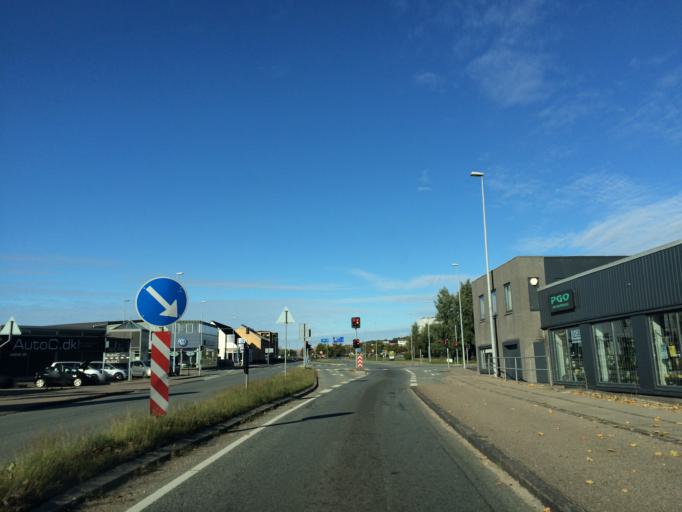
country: DK
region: Central Jutland
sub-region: Randers Kommune
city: Randers
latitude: 56.4537
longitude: 10.0465
